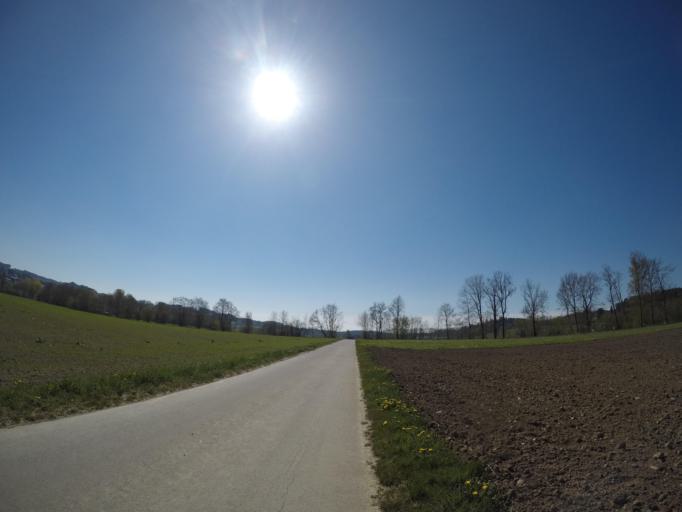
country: DE
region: Baden-Wuerttemberg
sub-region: Tuebingen Region
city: Wilhelmsdorf
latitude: 47.8343
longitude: 9.4484
